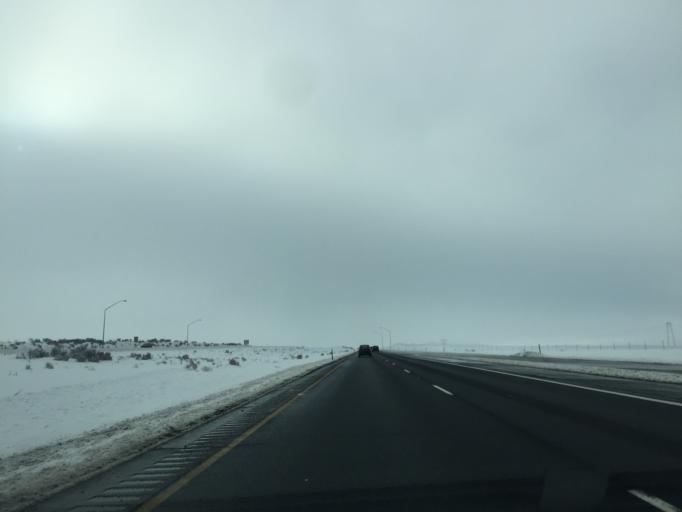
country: US
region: Washington
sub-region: Grant County
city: Quincy
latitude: 47.0188
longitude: -119.9467
